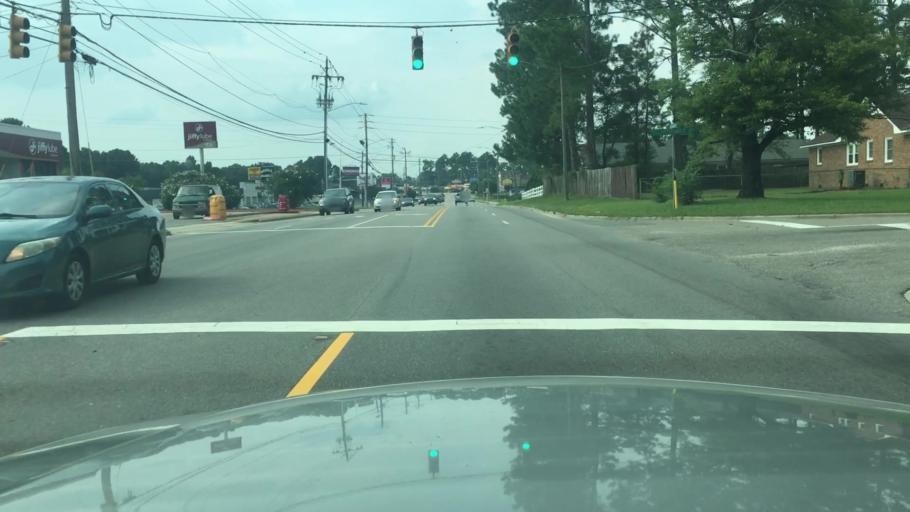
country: US
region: North Carolina
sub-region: Cumberland County
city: Fort Bragg
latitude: 35.0972
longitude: -78.9884
